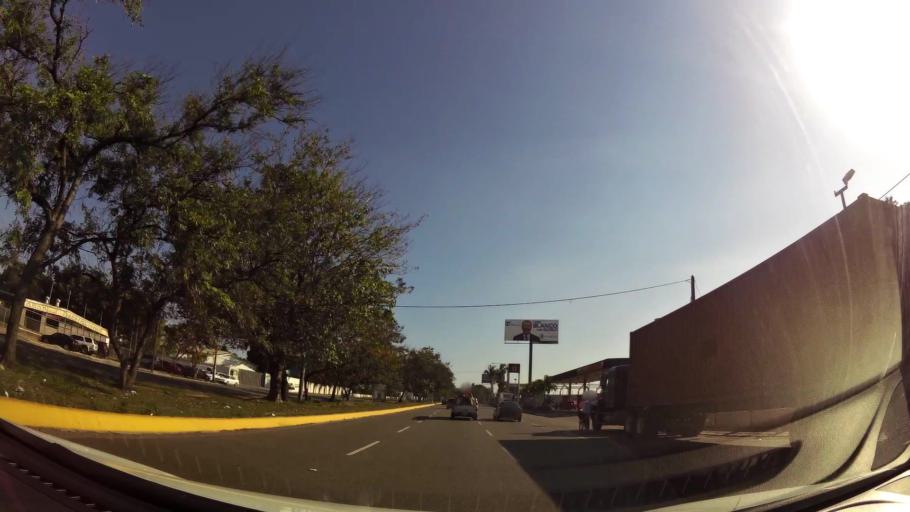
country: DO
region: Nacional
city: Bella Vista
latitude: 18.4745
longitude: -69.9681
